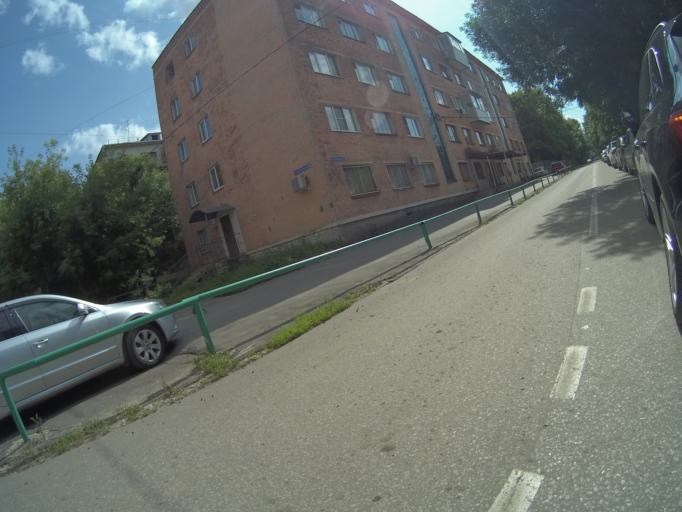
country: RU
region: Vladimir
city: Vladimir
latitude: 56.1428
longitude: 40.3991
